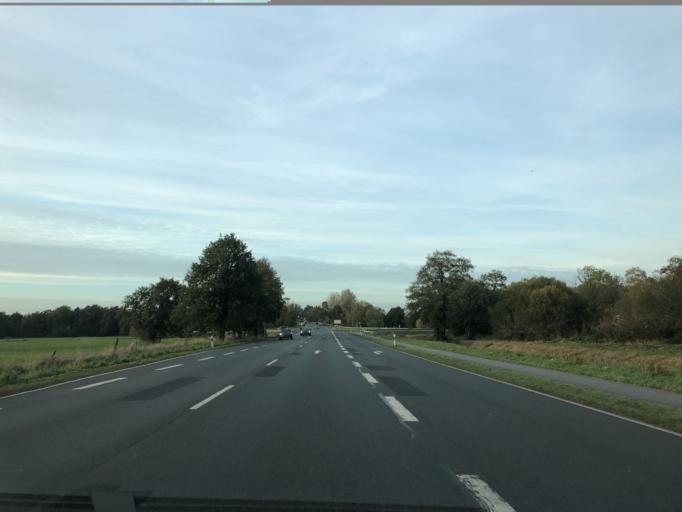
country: DE
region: Lower Saxony
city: Papenburg
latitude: 53.0783
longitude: 7.3797
